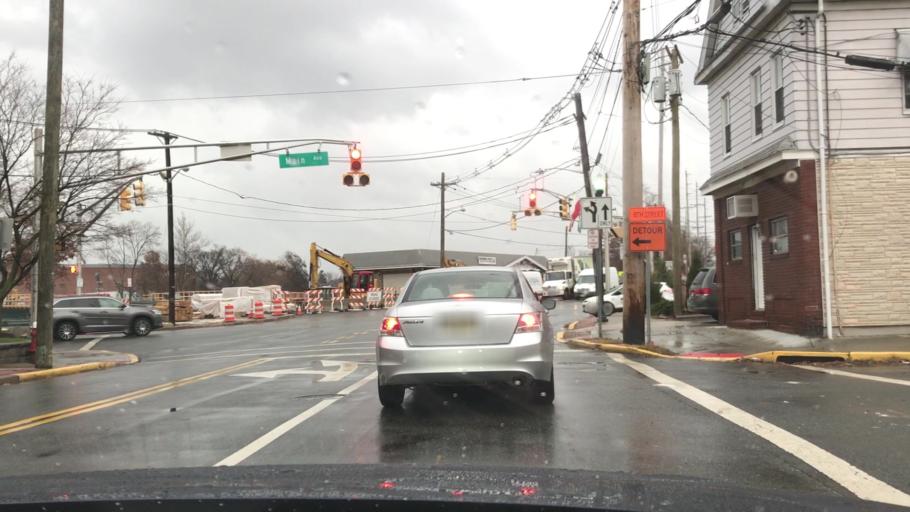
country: US
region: New Jersey
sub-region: Bergen County
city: Wallington
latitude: 40.8543
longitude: -74.1098
